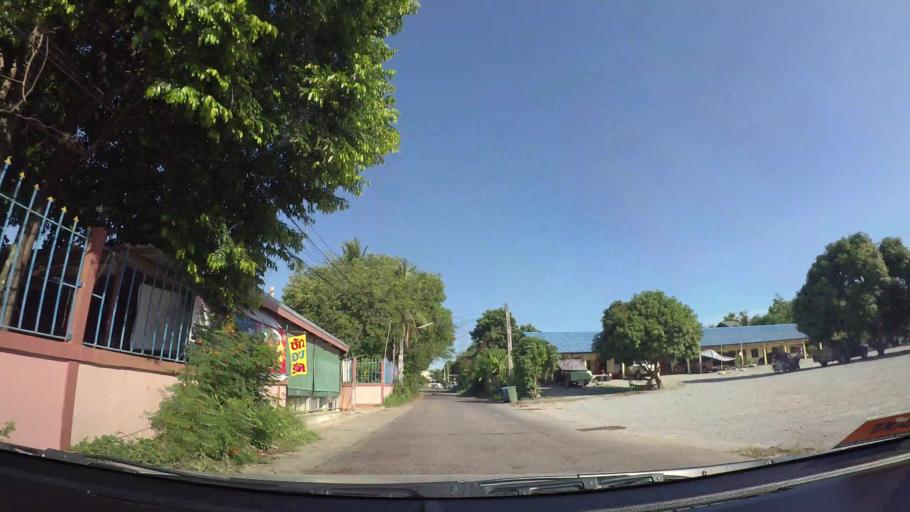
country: TH
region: Chon Buri
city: Si Racha
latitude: 13.1505
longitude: 100.9402
